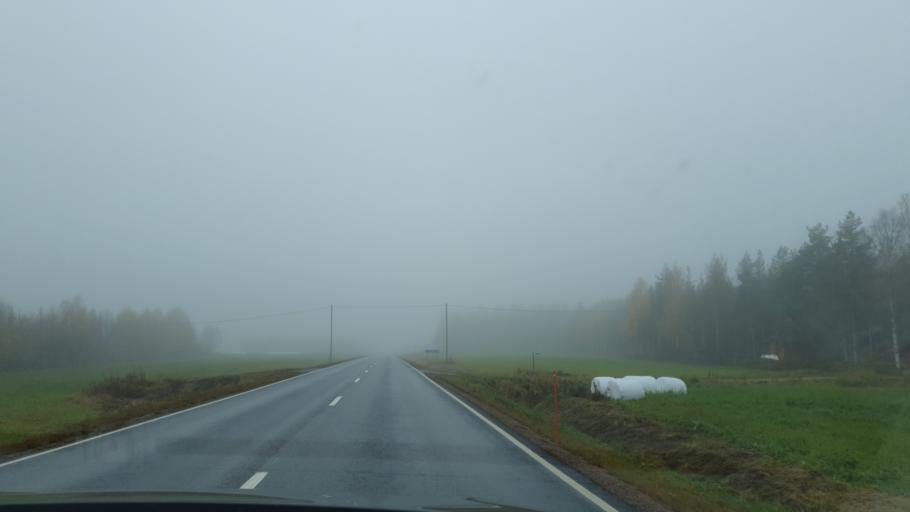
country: FI
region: Lapland
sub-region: Rovaniemi
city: Rovaniemi
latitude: 66.8024
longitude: 25.4135
